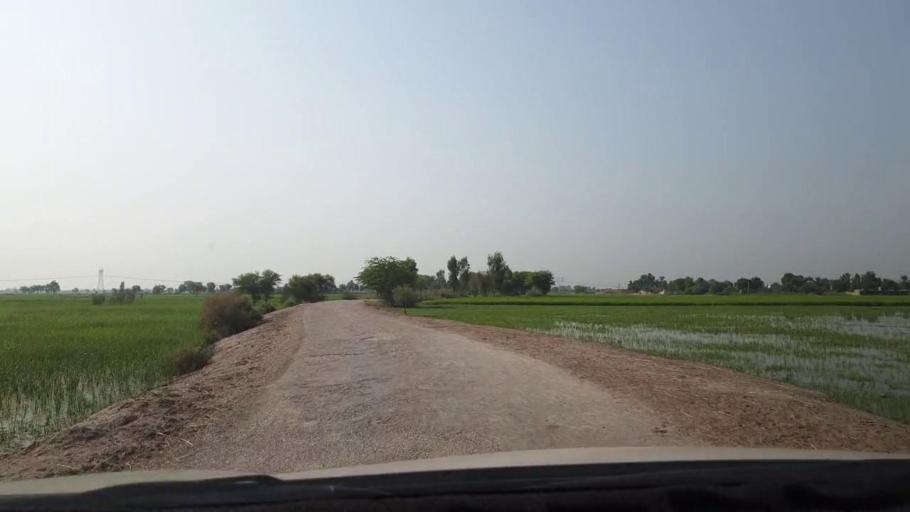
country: PK
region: Sindh
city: Goth Garelo
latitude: 27.4915
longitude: 68.1141
